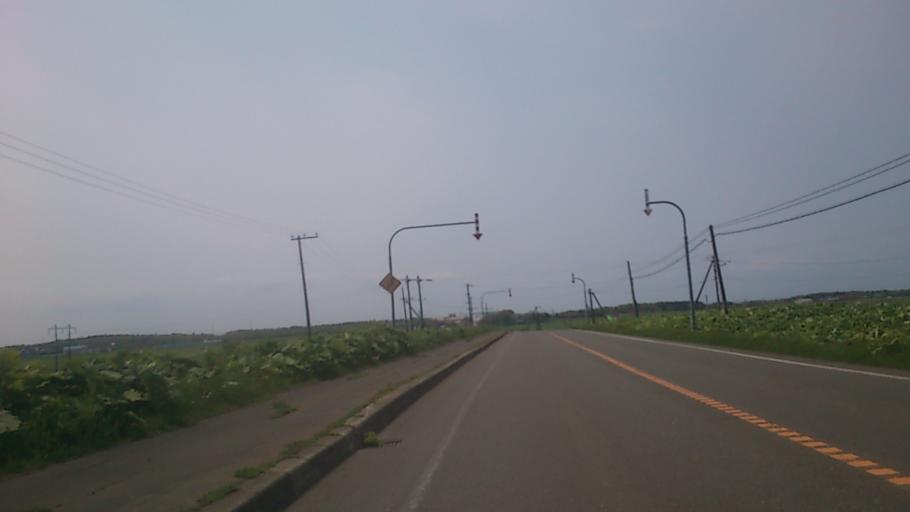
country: JP
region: Hokkaido
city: Nemuro
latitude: 43.2750
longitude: 145.5282
